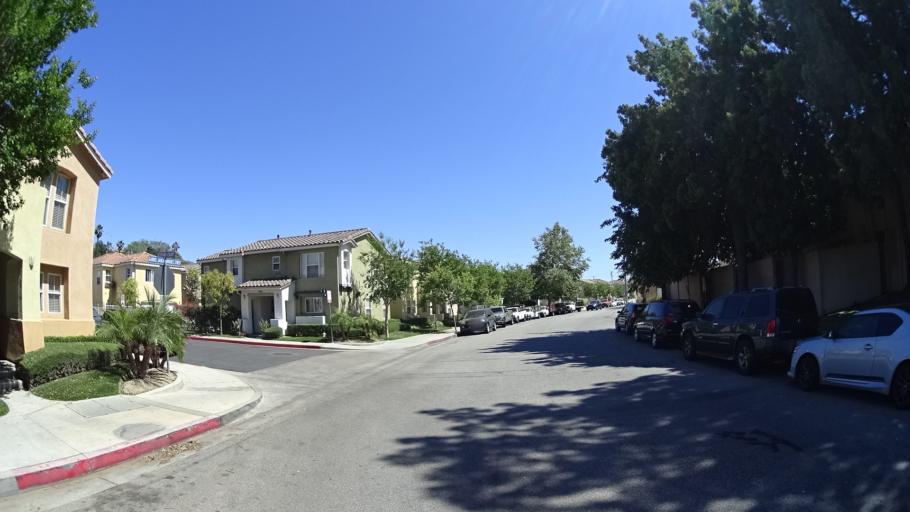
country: US
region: California
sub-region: Los Angeles County
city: Los Angeles
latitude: 34.0498
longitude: -118.2241
